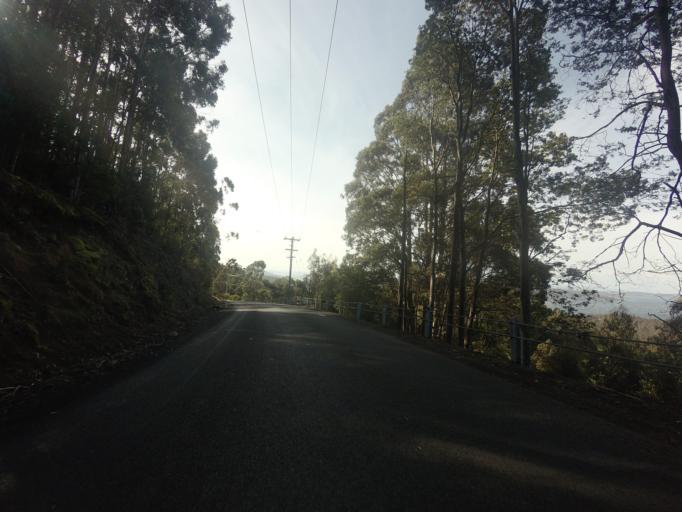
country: AU
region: Tasmania
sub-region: Kingborough
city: Kettering
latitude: -43.1689
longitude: 147.2062
